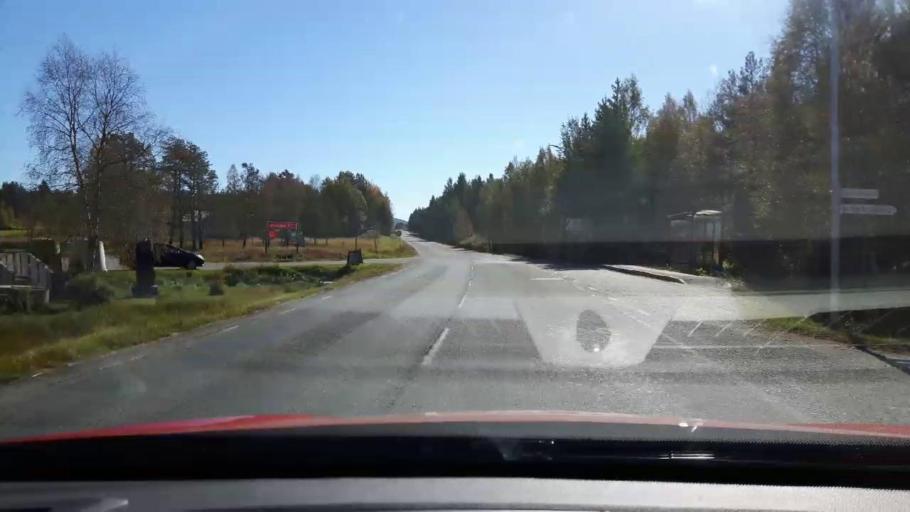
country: SE
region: Jaemtland
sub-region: Harjedalens Kommun
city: Sveg
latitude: 62.3097
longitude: 14.0415
